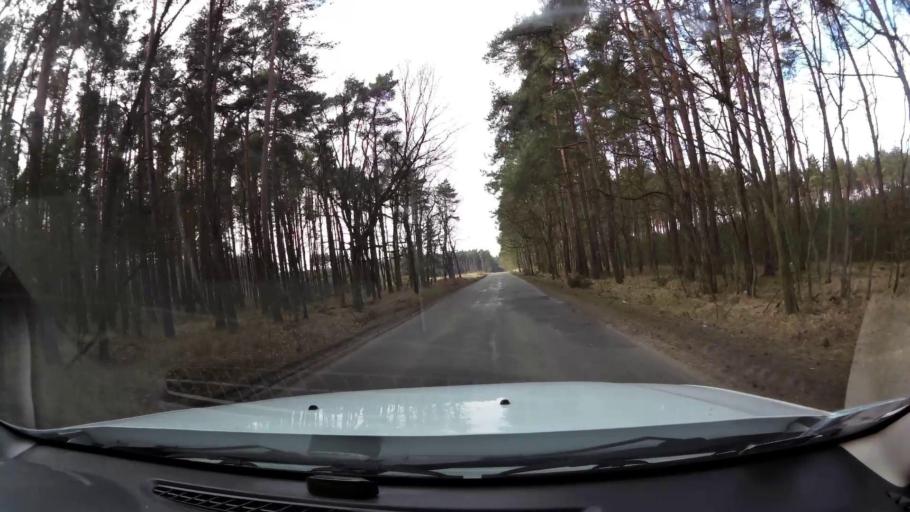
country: PL
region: West Pomeranian Voivodeship
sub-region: Powiat mysliborski
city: Debno
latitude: 52.8334
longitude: 14.6637
